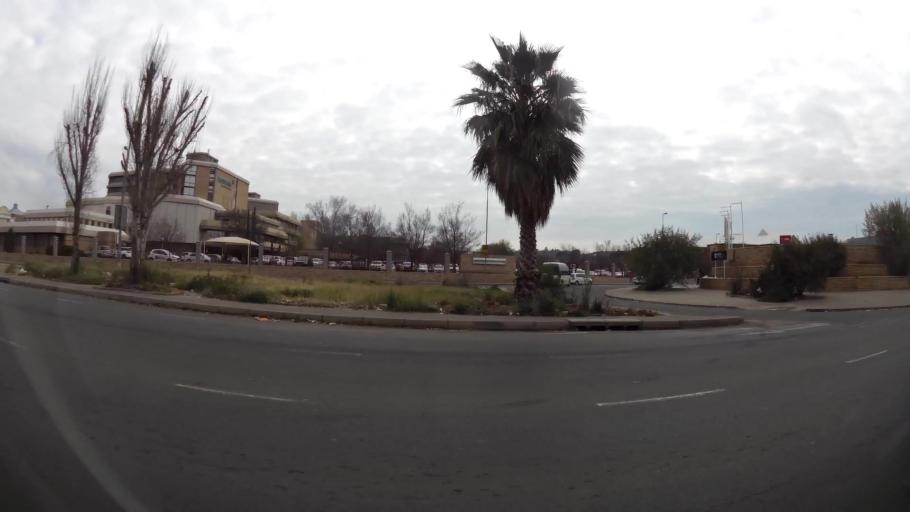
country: ZA
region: Orange Free State
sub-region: Mangaung Metropolitan Municipality
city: Bloemfontein
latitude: -29.1100
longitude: 26.2038
